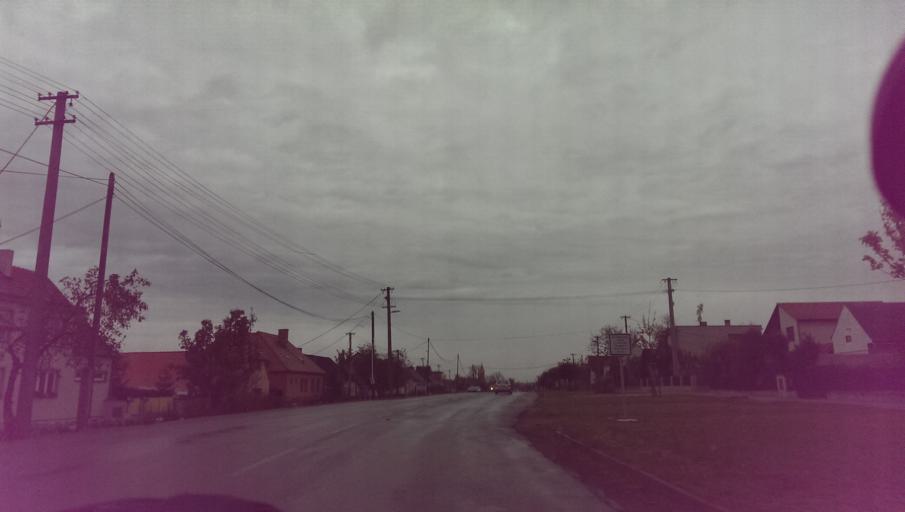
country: AT
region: Lower Austria
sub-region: Politischer Bezirk Hollabrunn
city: Hardegg
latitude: 48.9055
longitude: 15.8743
